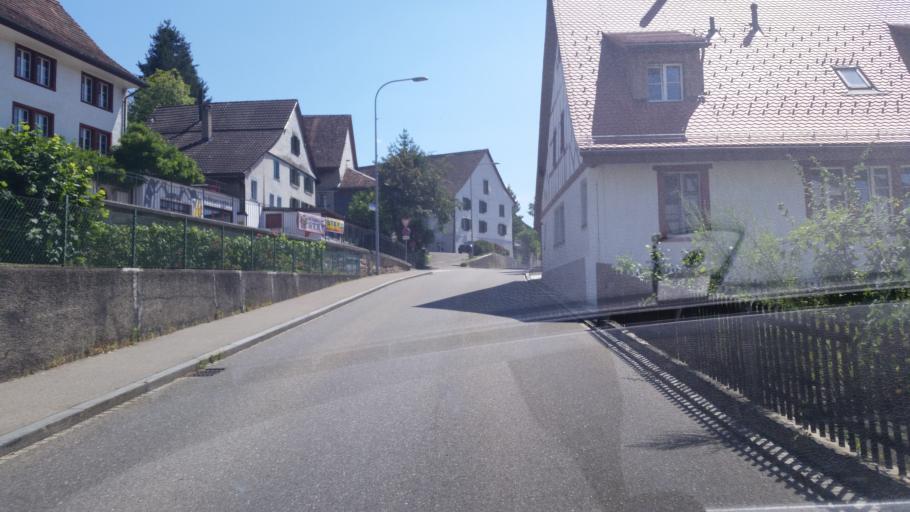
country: CH
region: Zurich
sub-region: Bezirk Buelach
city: Glattfelden
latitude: 47.5605
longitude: 8.4978
